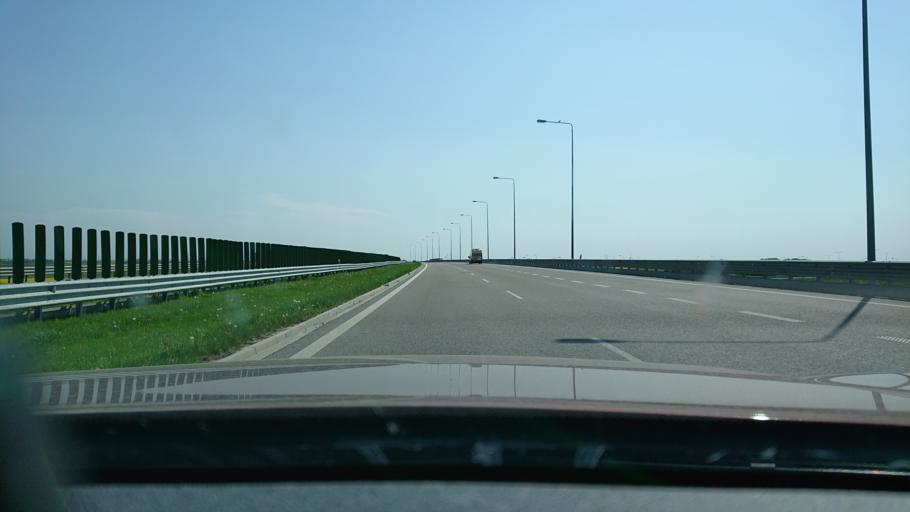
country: PL
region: Subcarpathian Voivodeship
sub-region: Powiat jaroslawski
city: Radymno
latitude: 49.9107
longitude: 22.8140
